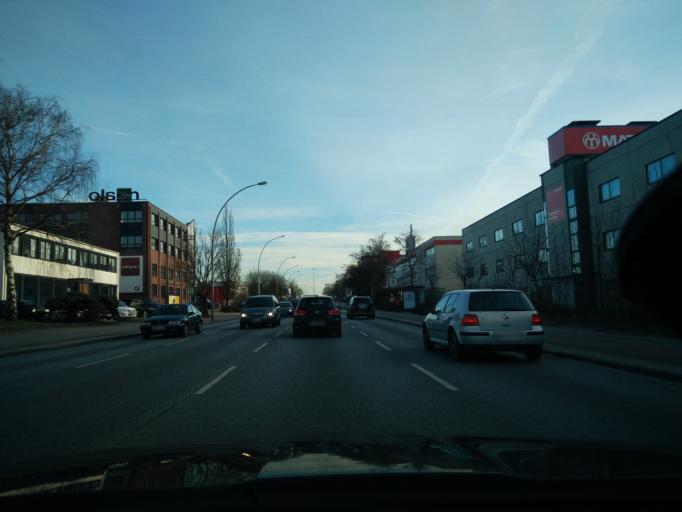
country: DE
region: Hamburg
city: Stellingen
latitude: 53.5804
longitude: 9.9180
